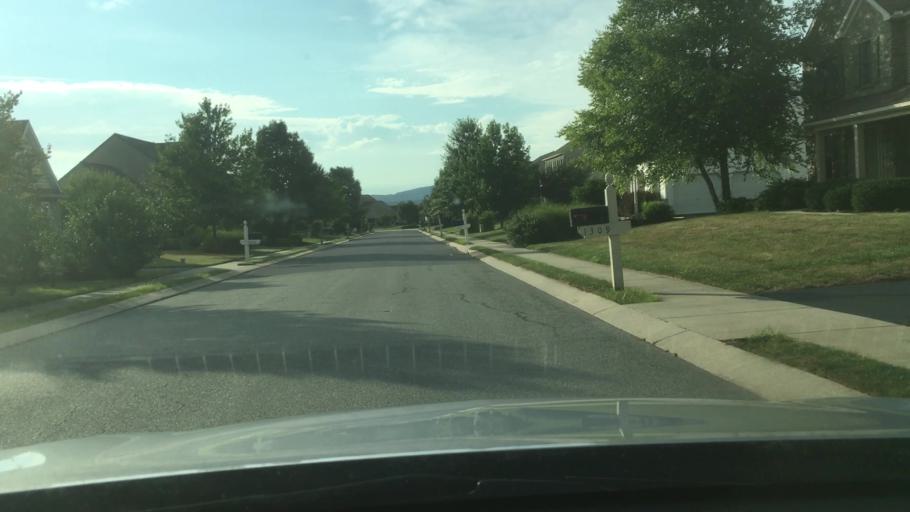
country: US
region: Pennsylvania
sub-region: York County
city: Shiloh
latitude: 39.9921
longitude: -76.7800
